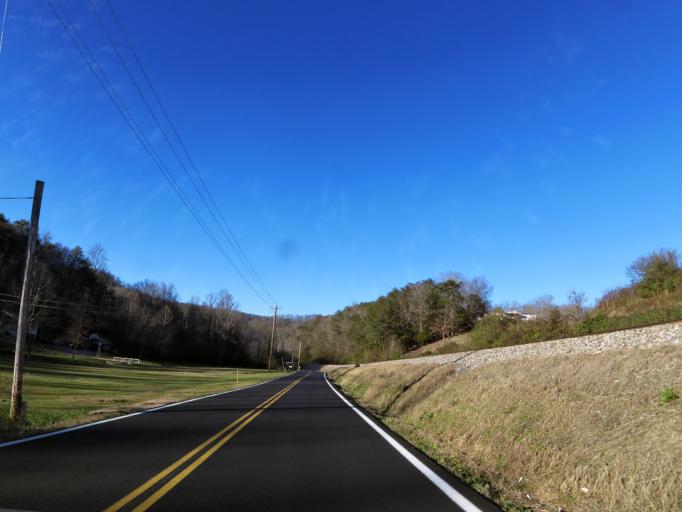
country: US
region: Tennessee
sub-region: Anderson County
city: Oak Ridge
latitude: 36.0666
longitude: -84.2459
